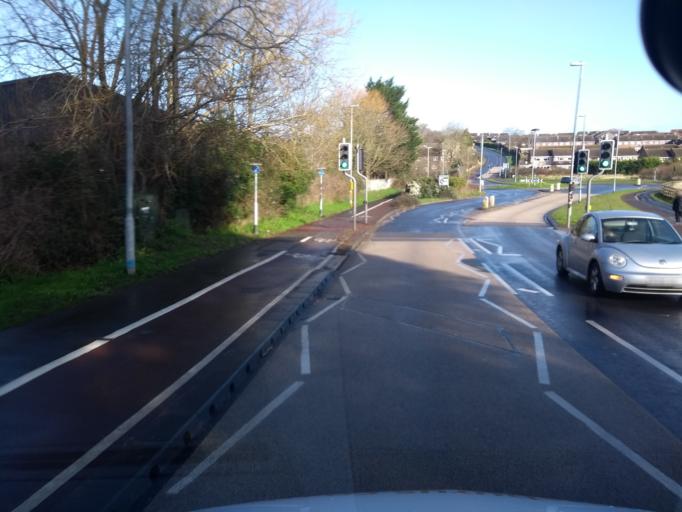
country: GB
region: England
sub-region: Somerset
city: Yeovil
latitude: 50.9537
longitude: -2.6097
